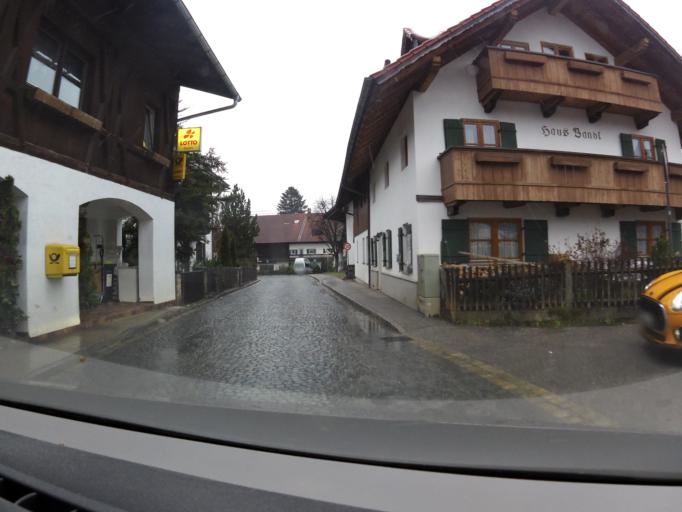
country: DE
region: Bavaria
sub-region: Upper Bavaria
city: Benediktbeuern
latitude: 47.7056
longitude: 11.4154
